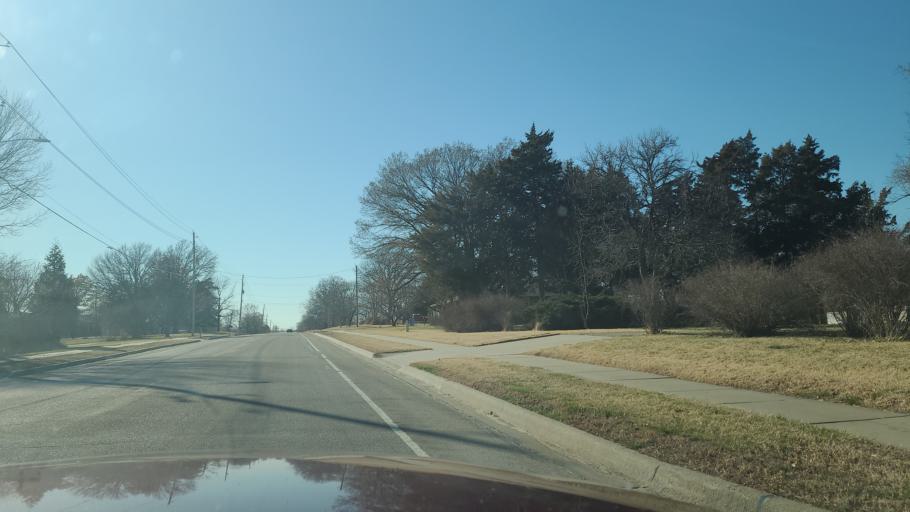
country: US
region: Kansas
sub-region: Douglas County
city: Lawrence
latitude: 38.9934
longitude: -95.2534
